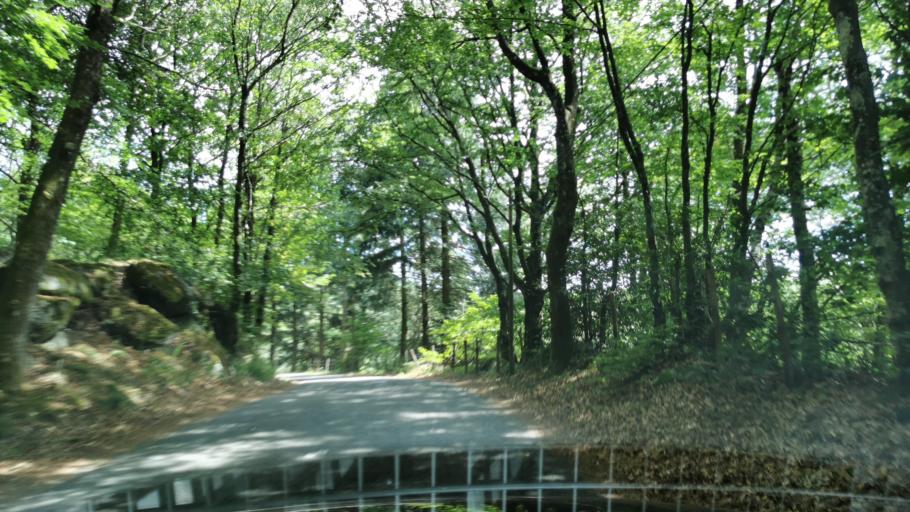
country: FR
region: Bourgogne
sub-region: Departement de Saone-et-Loire
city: Etang-sur-Arroux
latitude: 46.8096
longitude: 4.2567
